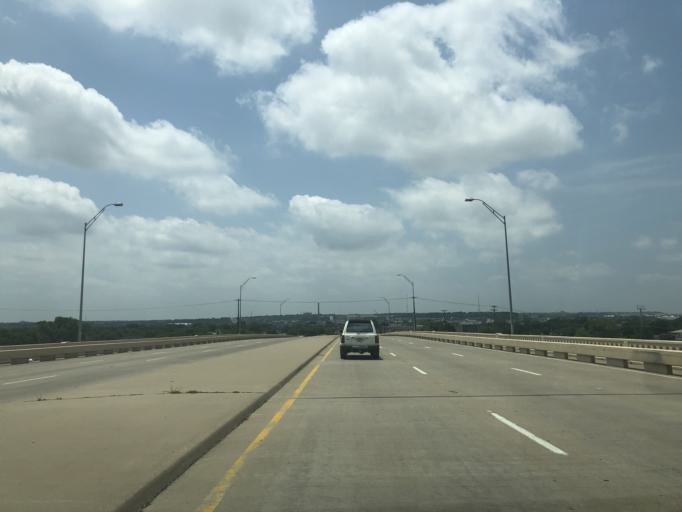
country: US
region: Texas
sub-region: Dallas County
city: Dallas
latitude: 32.7957
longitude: -96.8554
